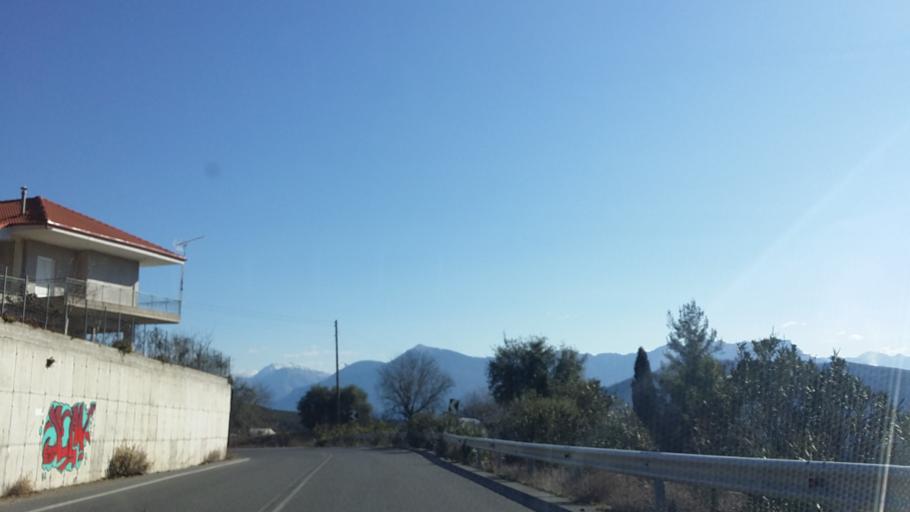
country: GR
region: Central Greece
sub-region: Nomos Evrytanias
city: Kerasochori
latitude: 38.9279
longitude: 21.4365
